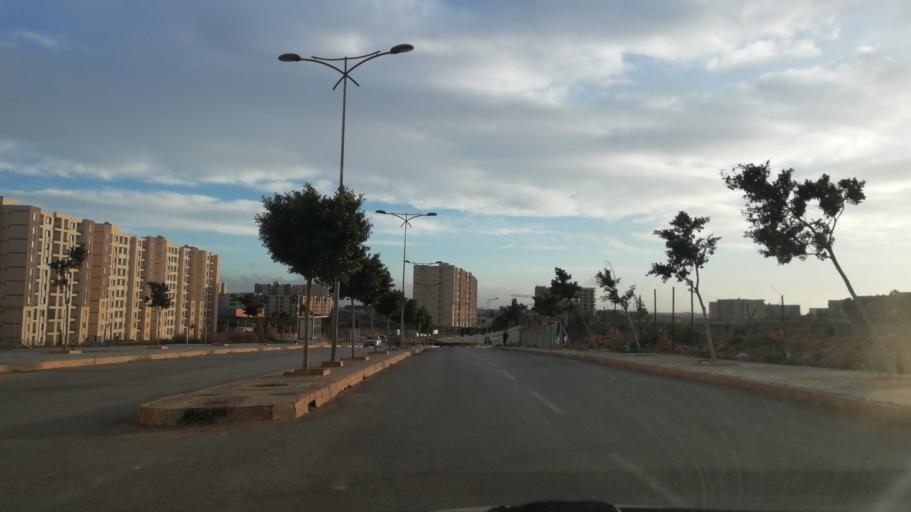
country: DZ
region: Oran
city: Bir el Djir
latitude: 35.6907
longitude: -0.5863
